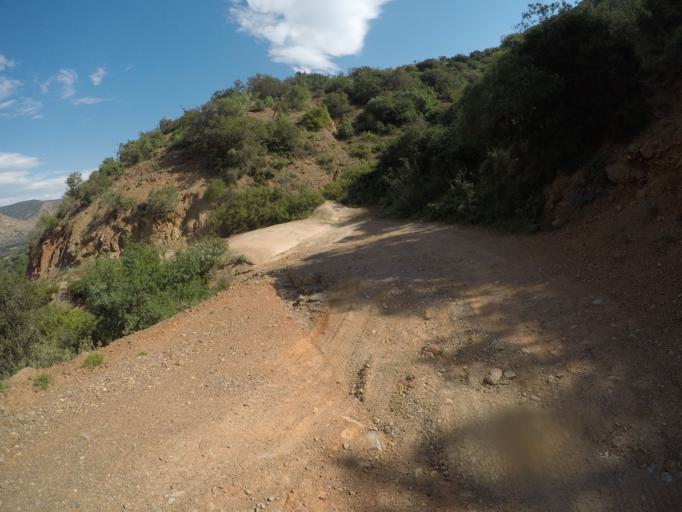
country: ZA
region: Eastern Cape
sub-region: Cacadu District Municipality
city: Kareedouw
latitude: -33.6583
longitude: 24.4008
